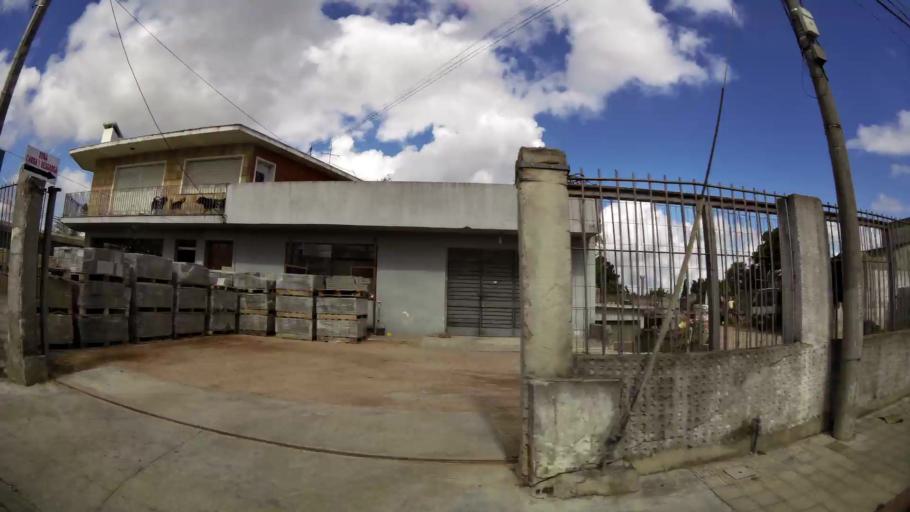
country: UY
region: Montevideo
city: Montevideo
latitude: -34.8460
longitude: -56.2224
